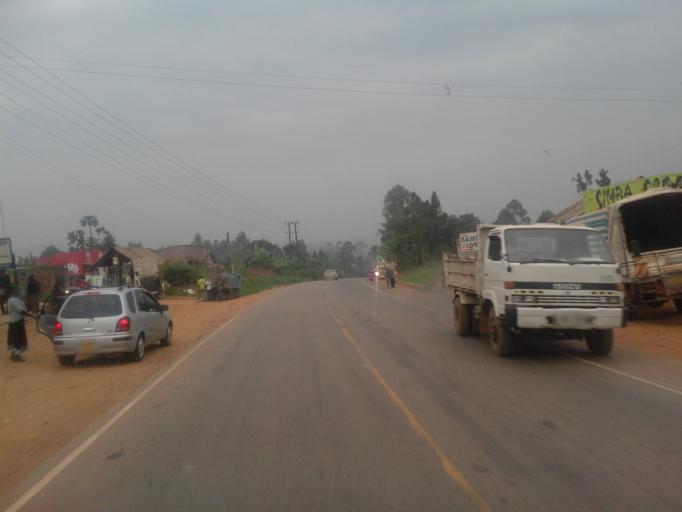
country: UG
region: Central Region
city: Lugazi
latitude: 0.3887
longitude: 32.8447
